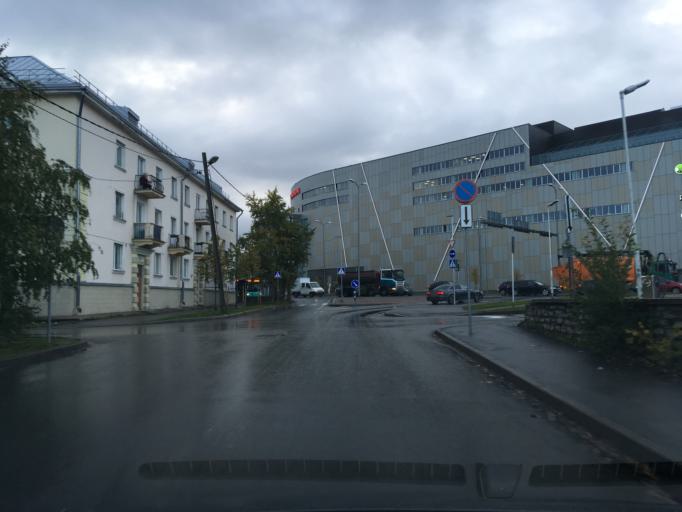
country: EE
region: Harju
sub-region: Tallinna linn
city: Tallinn
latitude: 59.4256
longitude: 24.7934
